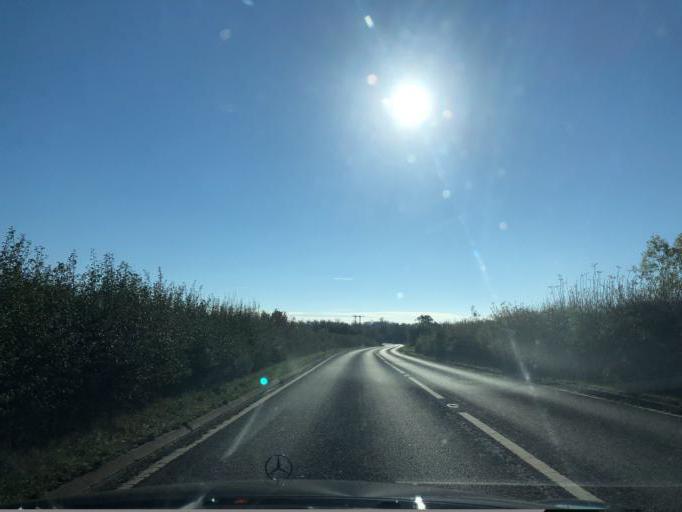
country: GB
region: England
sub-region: Warwickshire
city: Southam
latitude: 52.2363
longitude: -1.3909
